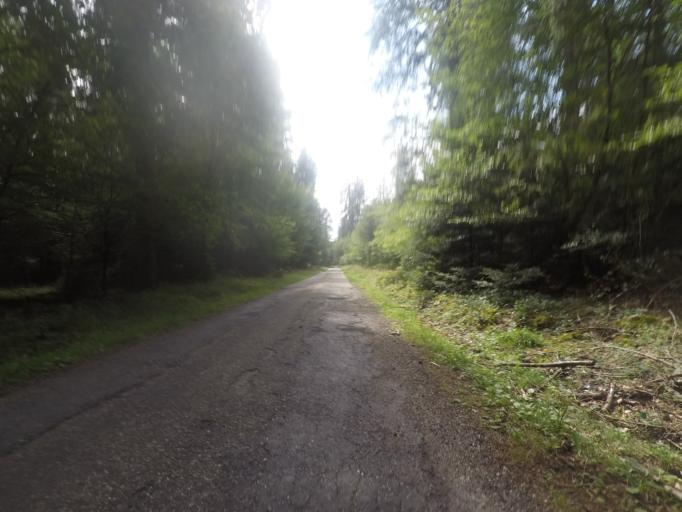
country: DE
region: Baden-Wuerttemberg
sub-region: Karlsruhe Region
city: Dobel
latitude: 48.7882
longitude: 8.4733
